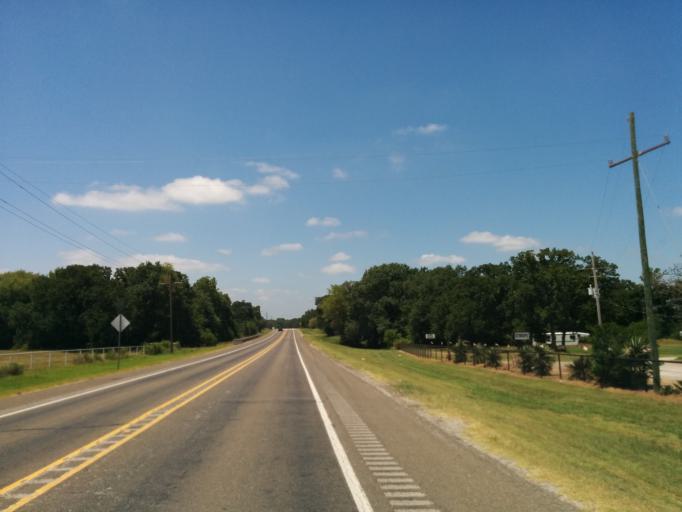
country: US
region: Texas
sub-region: Madison County
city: Madisonville
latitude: 30.9256
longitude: -95.9622
